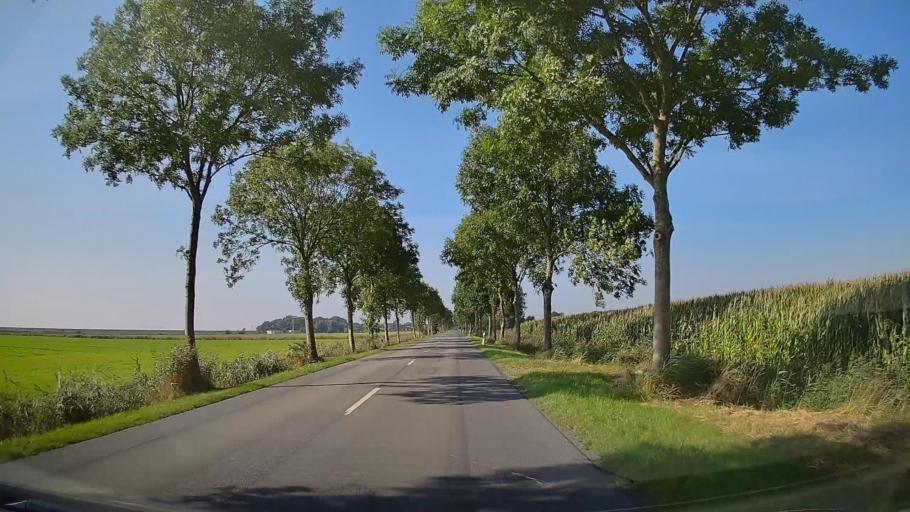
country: DE
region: Lower Saxony
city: Wremen
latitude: 53.6254
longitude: 8.5262
